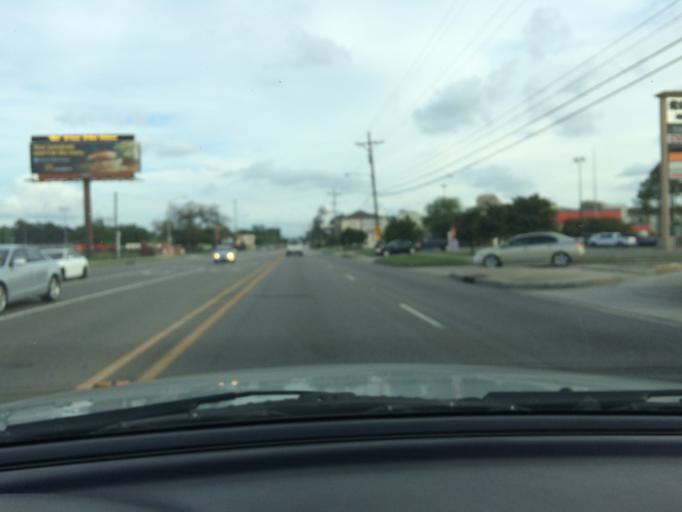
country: US
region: Louisiana
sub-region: Lafayette Parish
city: Lafayette
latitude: 30.2145
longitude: -92.0467
